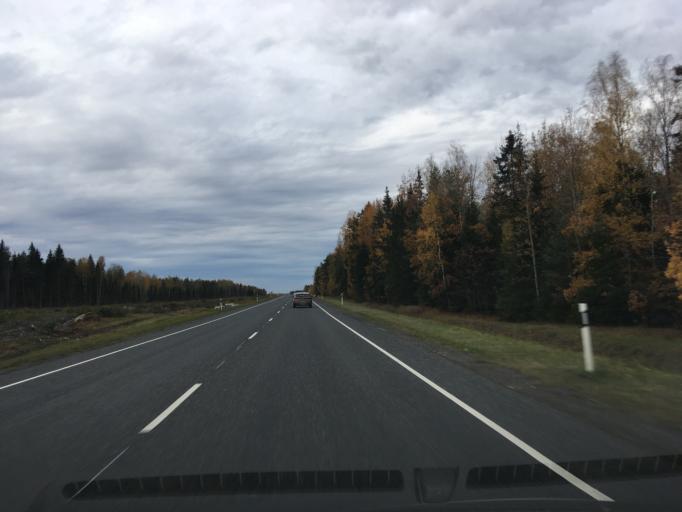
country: EE
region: Harju
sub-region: Nissi vald
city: Turba
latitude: 58.9550
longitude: 24.0787
